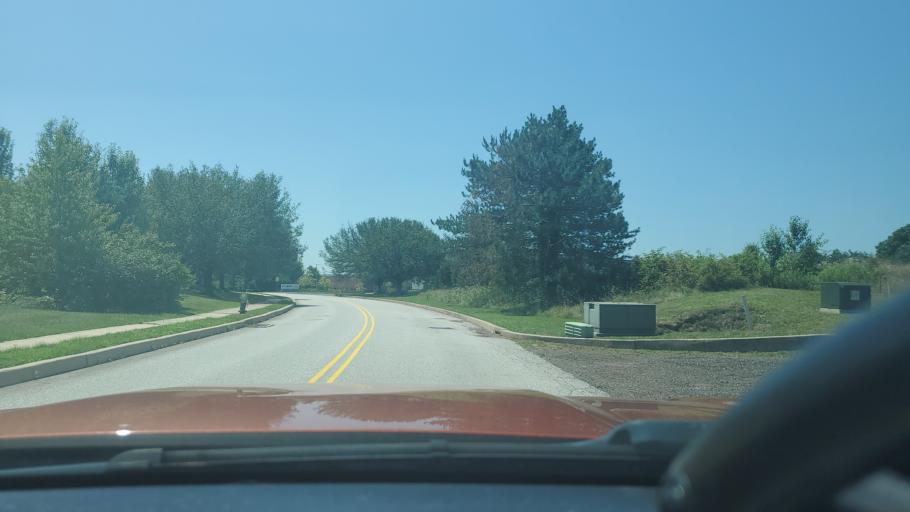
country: US
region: Pennsylvania
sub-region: Montgomery County
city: Limerick
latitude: 40.2211
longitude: -75.5568
